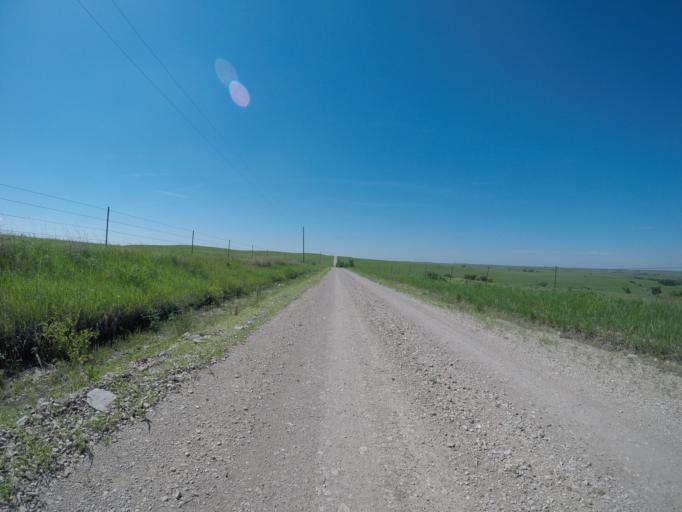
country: US
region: Kansas
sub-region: Wabaunsee County
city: Alma
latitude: 39.0077
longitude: -96.1783
